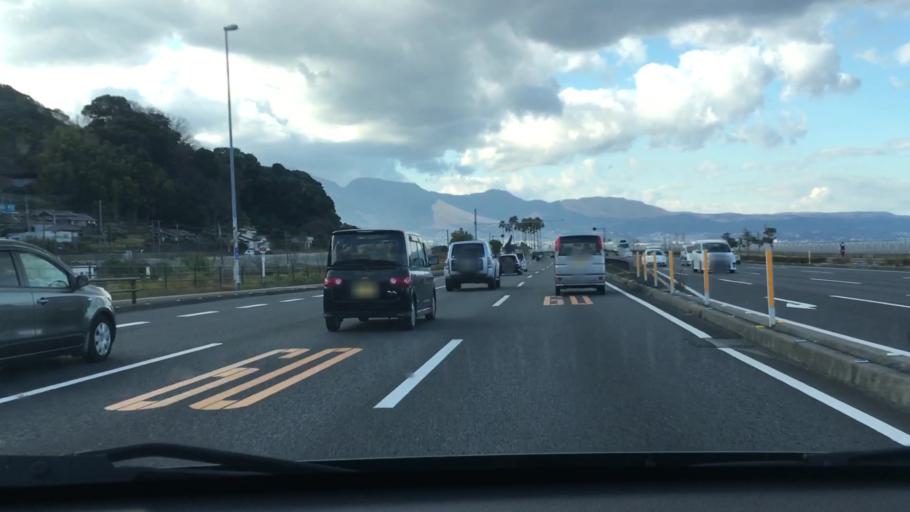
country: JP
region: Oita
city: Oita
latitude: 33.2537
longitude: 131.5636
